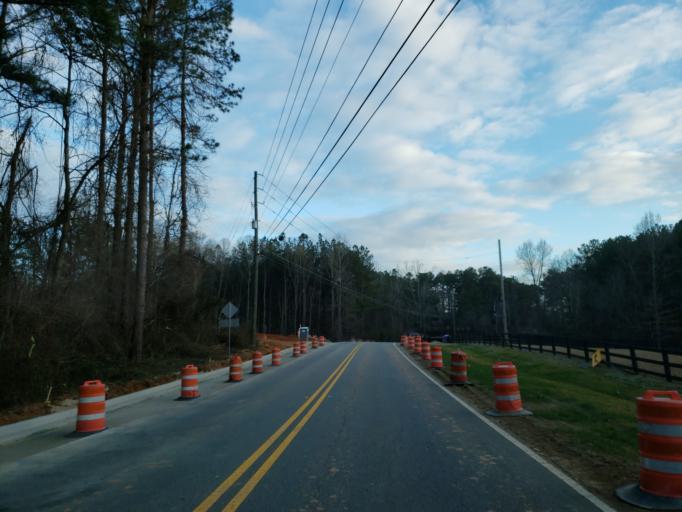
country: US
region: Georgia
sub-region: Cobb County
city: Acworth
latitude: 34.0030
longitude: -84.6768
